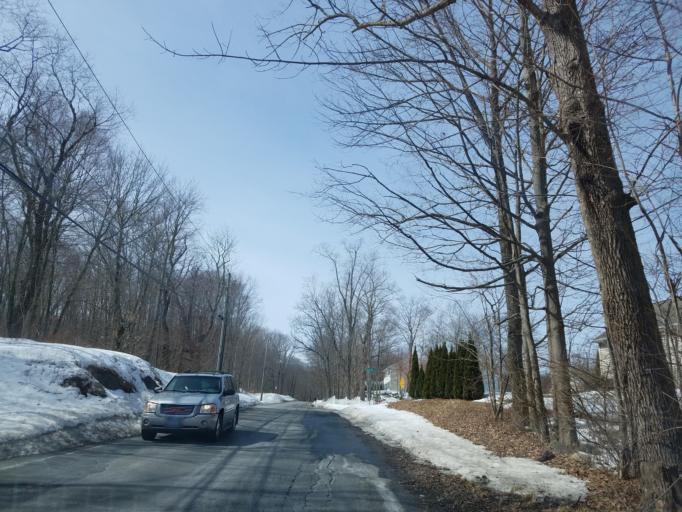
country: US
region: Connecticut
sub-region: Litchfield County
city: West Torrington
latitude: 41.8025
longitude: -73.1498
